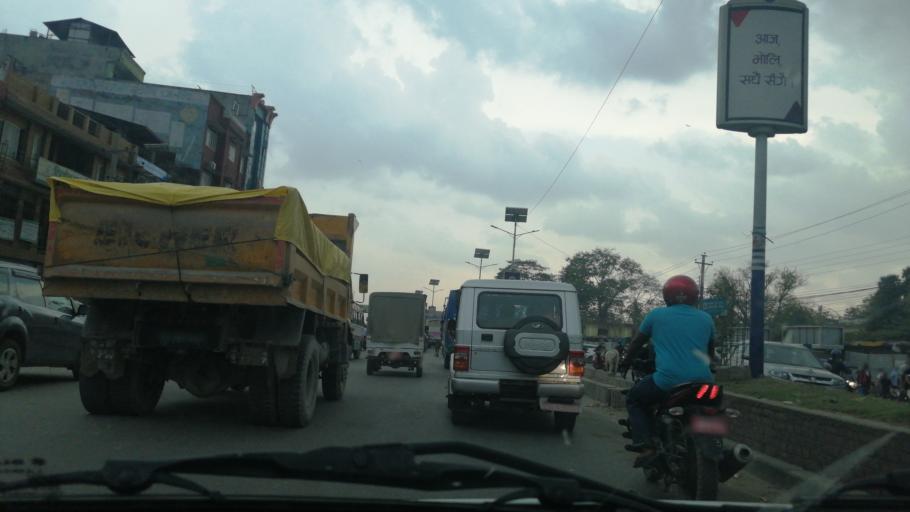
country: NP
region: Western Region
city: Butwal
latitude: 27.6973
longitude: 83.4652
